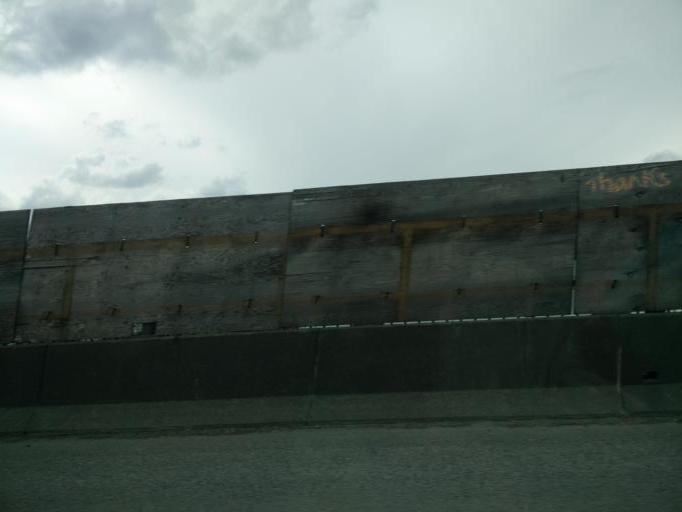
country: CA
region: British Columbia
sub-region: Fraser Valley Regional District
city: North Vancouver
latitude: 49.2948
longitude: -123.0264
